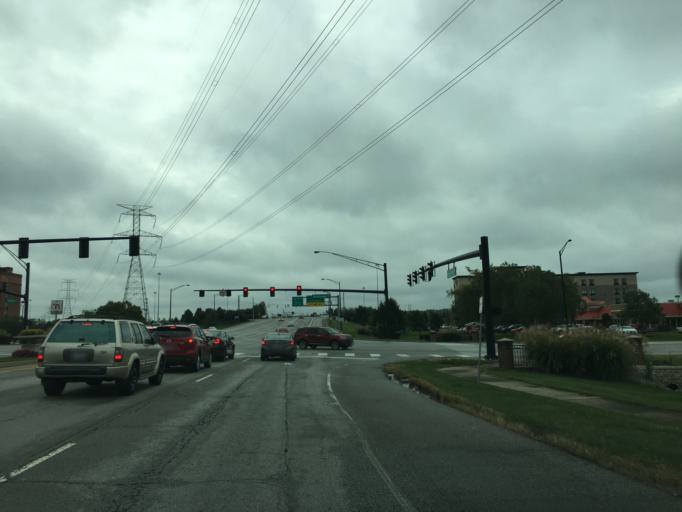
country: US
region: Ohio
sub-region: Butler County
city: Beckett Ridge
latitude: 39.3241
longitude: -84.4286
